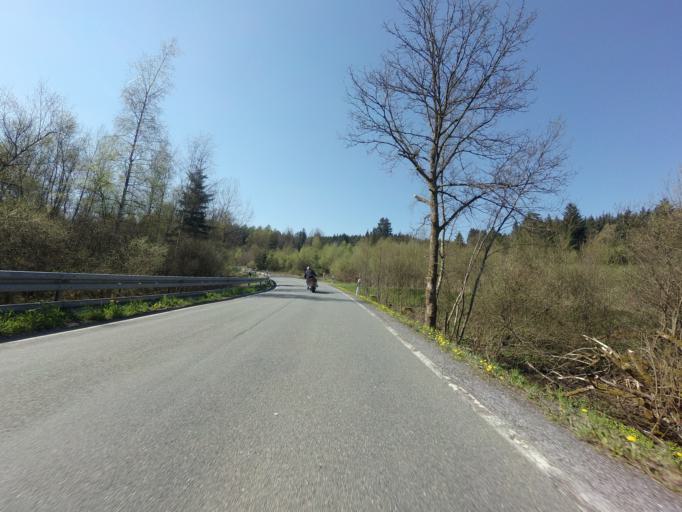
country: DE
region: North Rhine-Westphalia
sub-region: Regierungsbezirk Arnsberg
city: Herscheid
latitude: 51.0996
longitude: 7.7468
